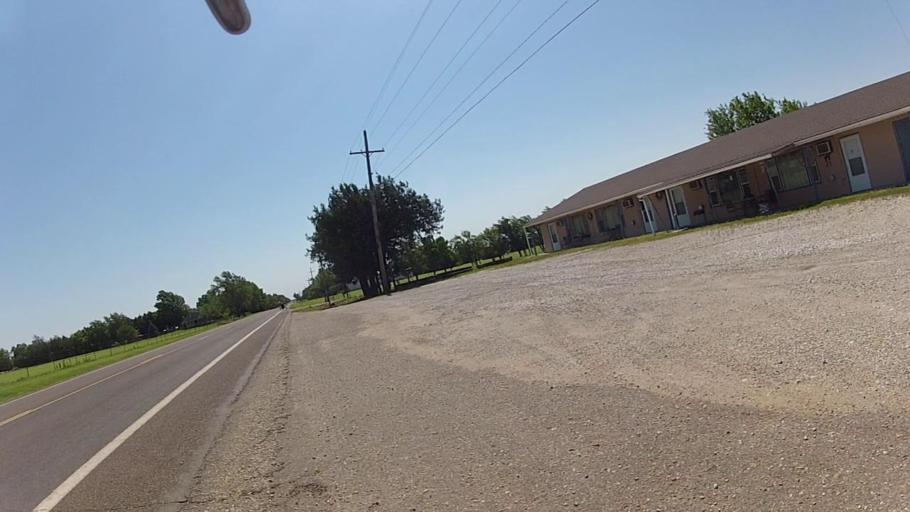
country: US
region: Kansas
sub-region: Sumner County
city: Caldwell
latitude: 37.0324
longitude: -97.5958
